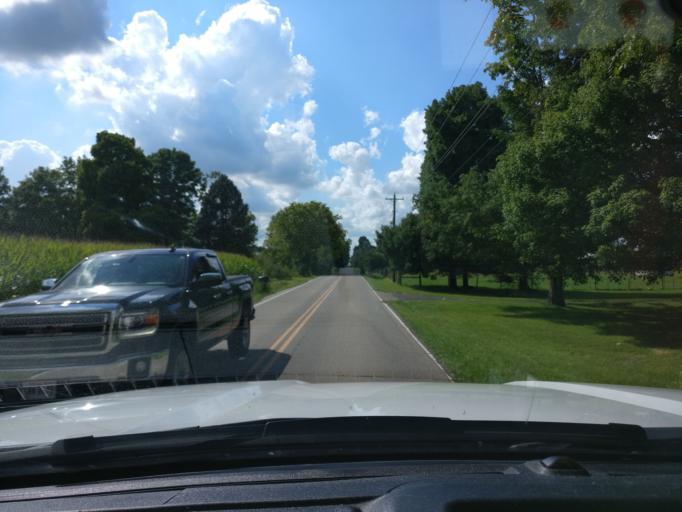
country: US
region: Ohio
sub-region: Warren County
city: Springboro
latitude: 39.5053
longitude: -84.2213
